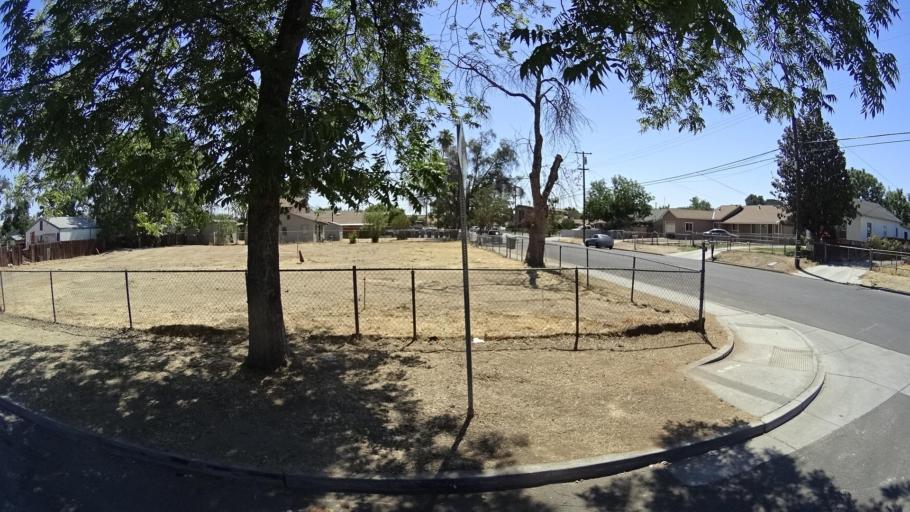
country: US
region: California
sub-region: Fresno County
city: Fresno
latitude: 36.7597
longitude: -119.7534
